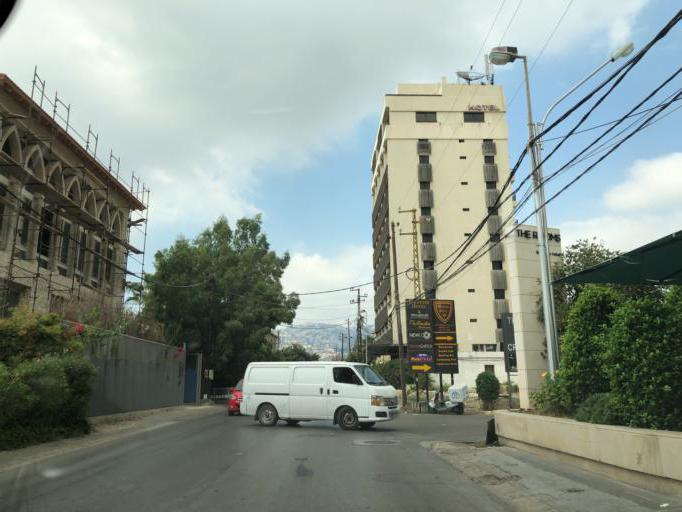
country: LB
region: Mont-Liban
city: Djounie
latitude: 33.9910
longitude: 35.6390
